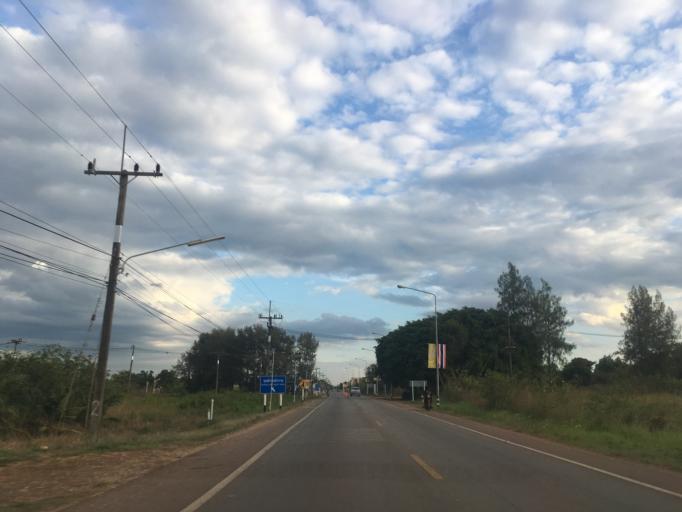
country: TH
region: Chanthaburi
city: Na Yai Am
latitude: 12.7165
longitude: 101.7685
